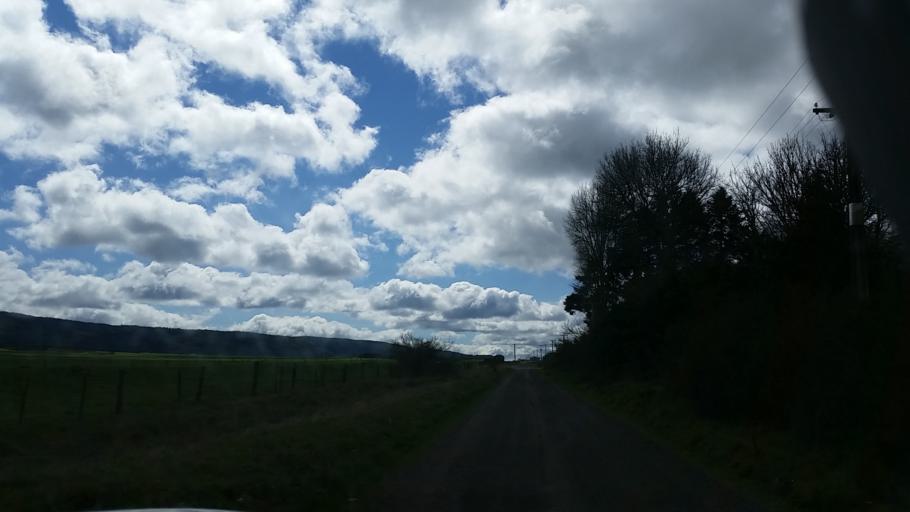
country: NZ
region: Bay of Plenty
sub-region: Whakatane District
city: Murupara
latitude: -38.2837
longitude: 176.5509
